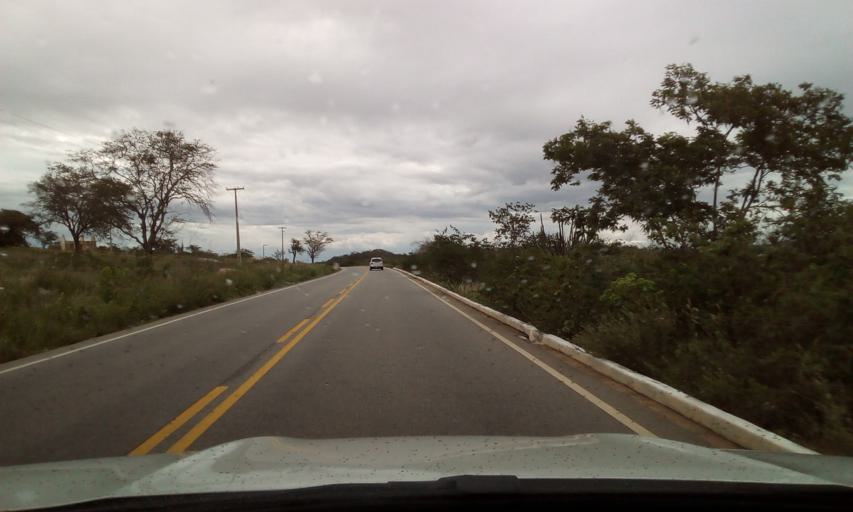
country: BR
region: Paraiba
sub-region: Picui
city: Picui
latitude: -6.5663
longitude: -36.2766
